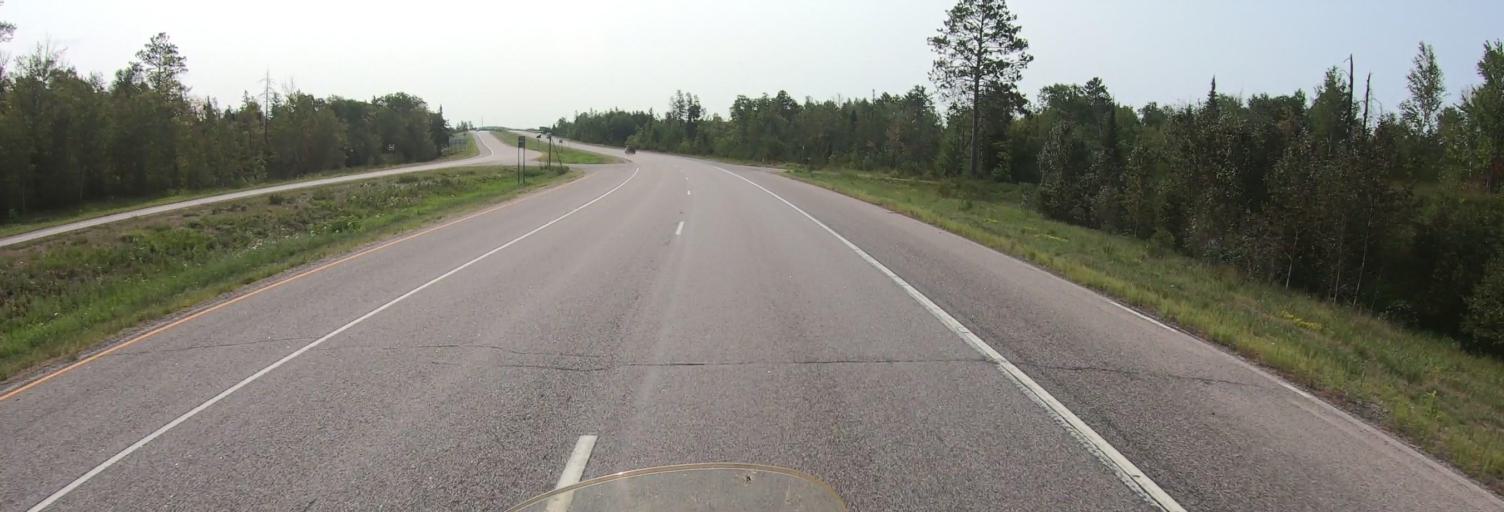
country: US
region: Minnesota
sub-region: Saint Louis County
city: Parkville
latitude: 47.5940
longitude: -92.5534
